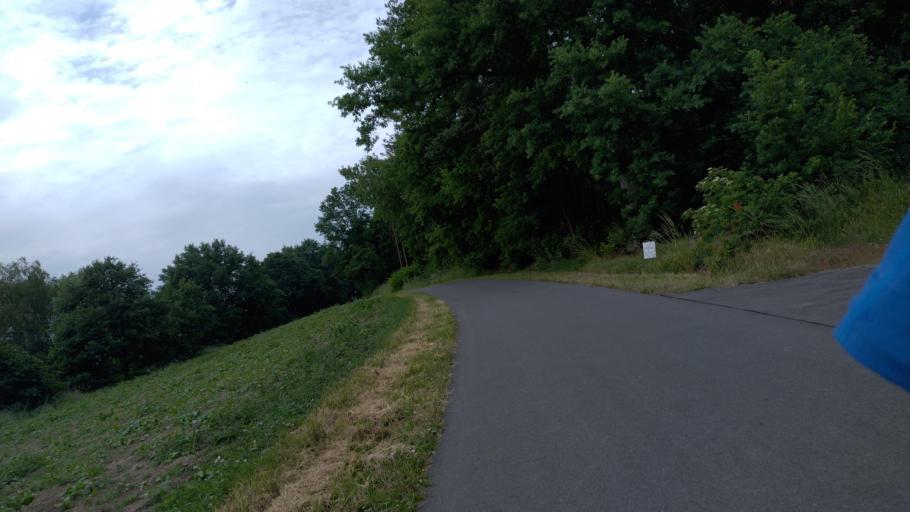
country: DE
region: Bavaria
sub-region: Upper Franconia
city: Harsdorf
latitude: 50.0172
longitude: 11.5781
